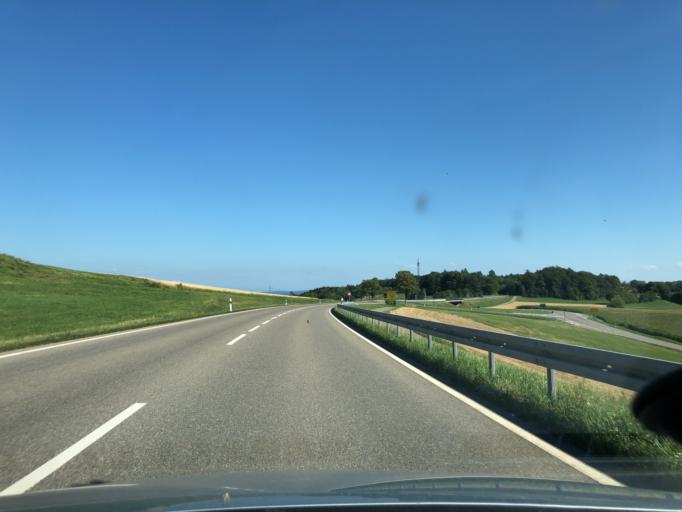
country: DE
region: Baden-Wuerttemberg
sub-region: Freiburg Region
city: Dogern
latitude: 47.6643
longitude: 8.1618
